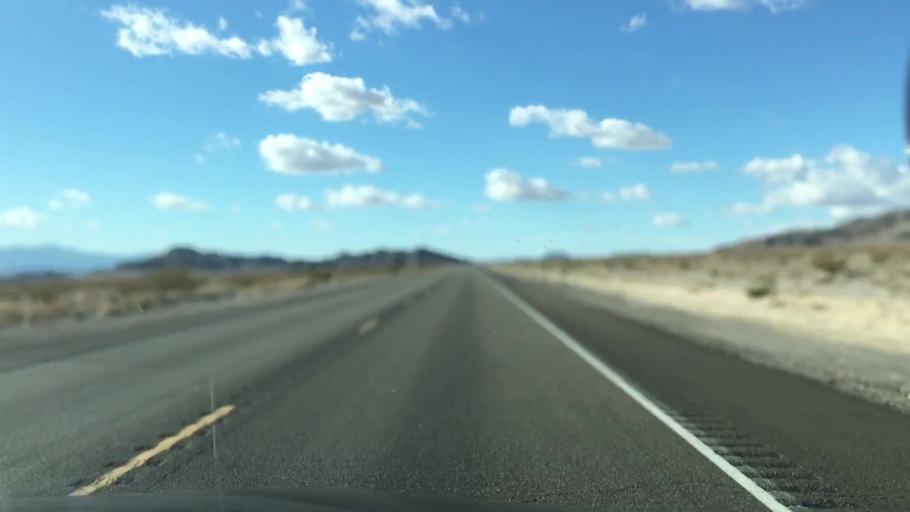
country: US
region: Nevada
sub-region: Nye County
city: Pahrump
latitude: 36.5718
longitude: -116.1725
